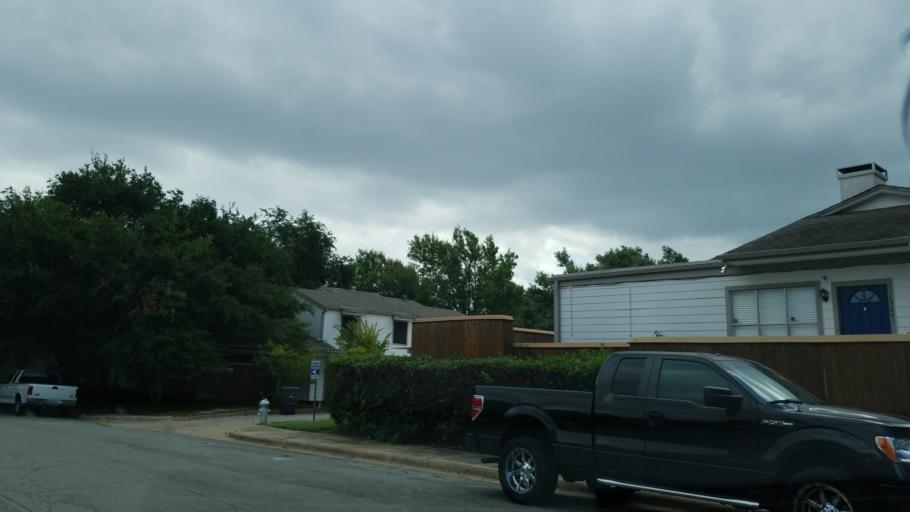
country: US
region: Texas
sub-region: Dallas County
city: Richardson
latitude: 32.9335
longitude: -96.7673
